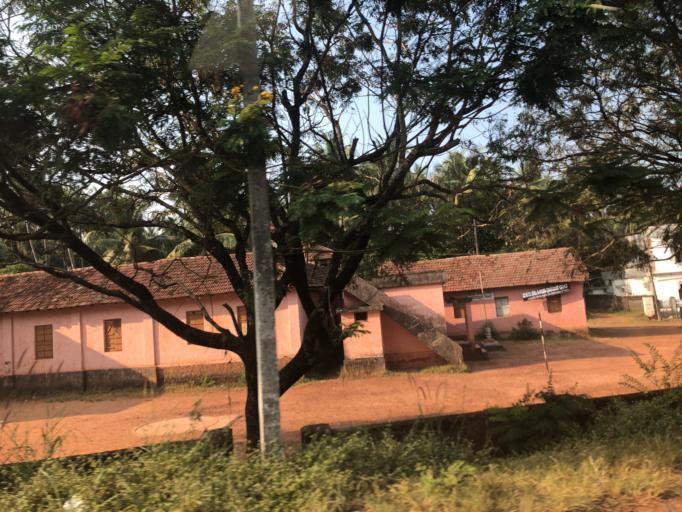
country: IN
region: Karnataka
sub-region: Dakshina Kannada
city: Ullal
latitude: 12.8198
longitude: 74.8692
